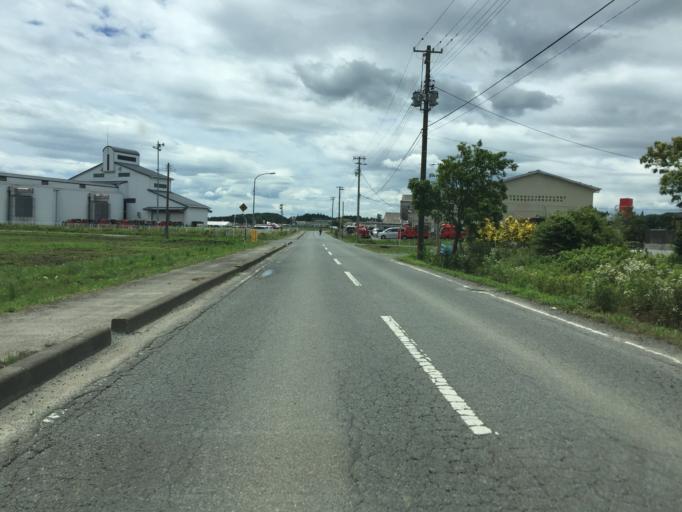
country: JP
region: Fukushima
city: Namie
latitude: 37.6248
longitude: 141.0004
